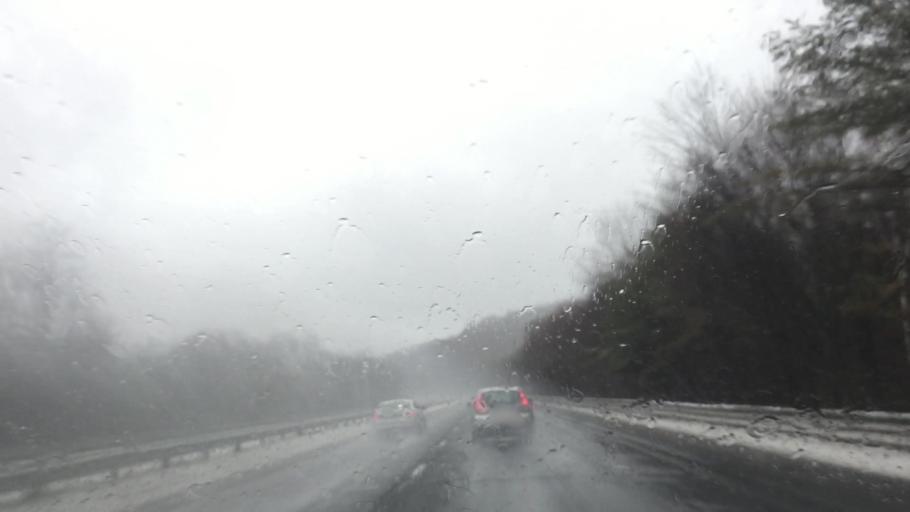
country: US
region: Massachusetts
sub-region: Hampden County
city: Granville
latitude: 42.1704
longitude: -72.8765
